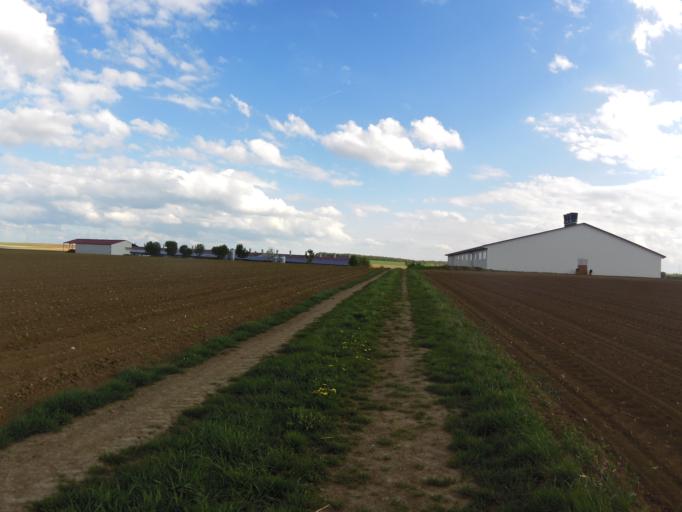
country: DE
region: Bavaria
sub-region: Regierungsbezirk Unterfranken
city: Unterpleichfeld
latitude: 49.8640
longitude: 10.0620
